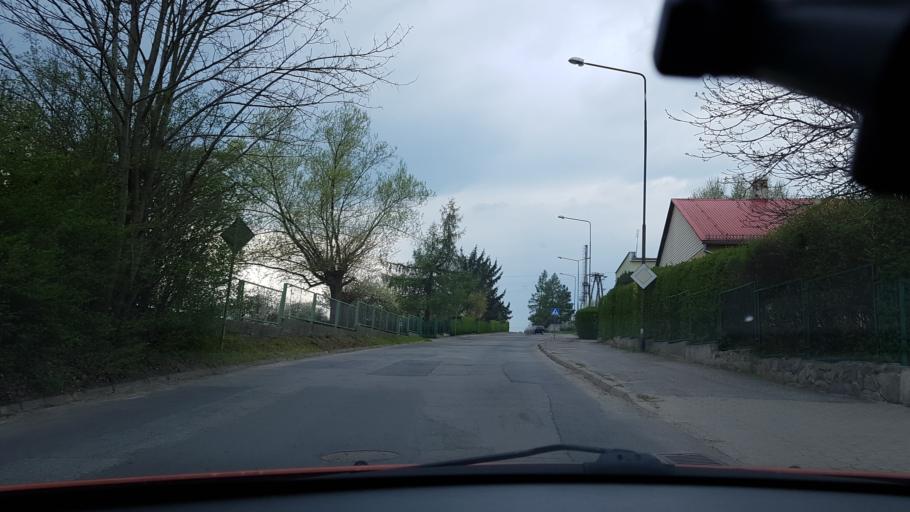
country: PL
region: Lower Silesian Voivodeship
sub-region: Powiat klodzki
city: Klodzko
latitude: 50.4301
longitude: 16.6445
